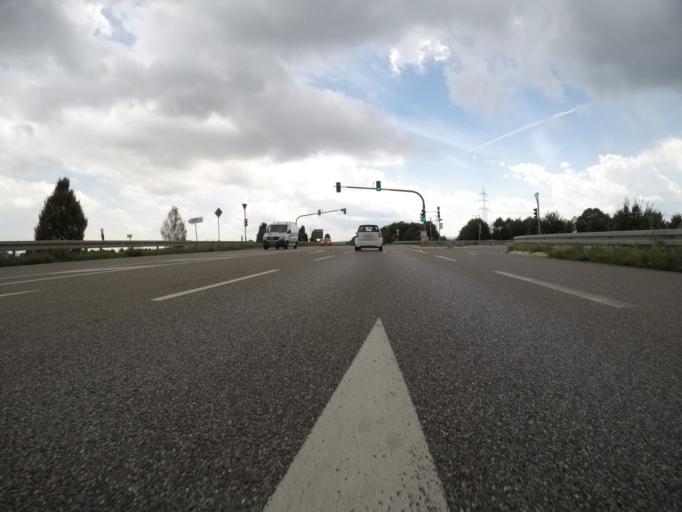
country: DE
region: Baden-Wuerttemberg
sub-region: Regierungsbezirk Stuttgart
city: Schwieberdingen
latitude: 48.8861
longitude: 9.0937
